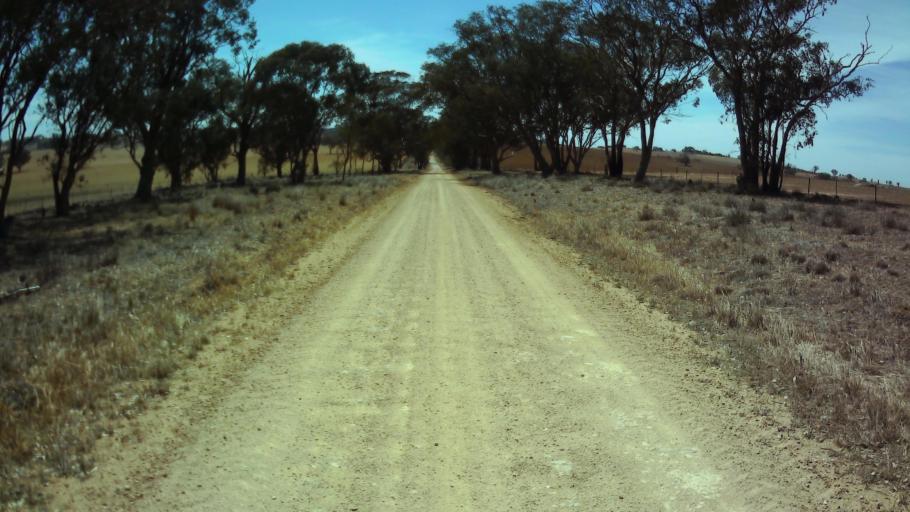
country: AU
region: New South Wales
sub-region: Weddin
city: Grenfell
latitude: -33.9430
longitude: 148.1441
